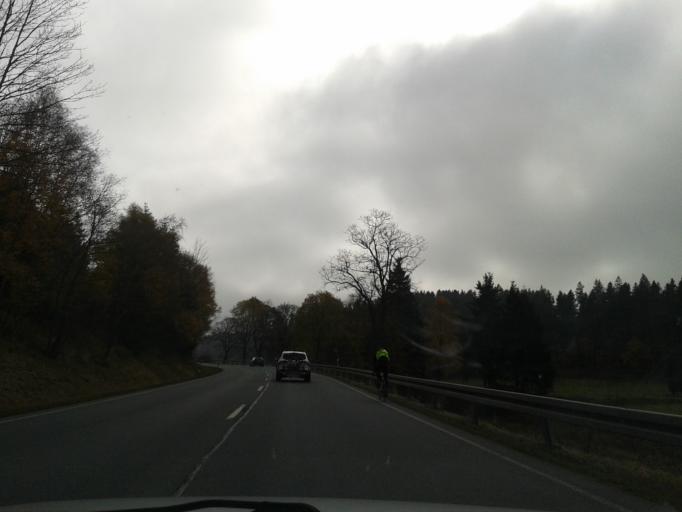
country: DE
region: North Rhine-Westphalia
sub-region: Regierungsbezirk Arnsberg
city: Winterberg
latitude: 51.2266
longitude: 8.5340
